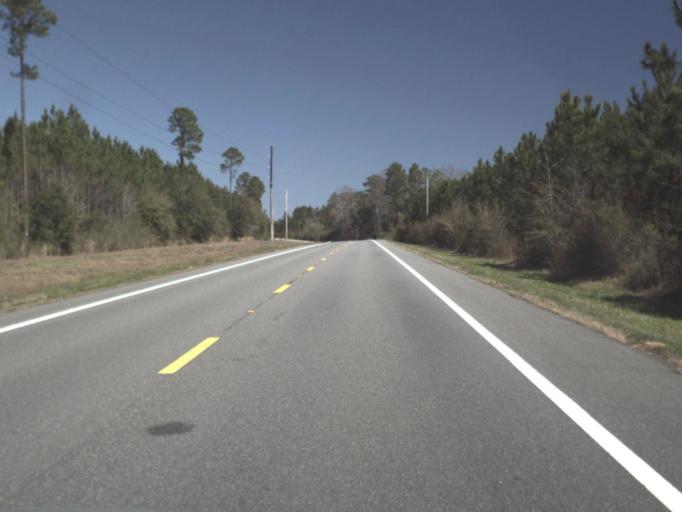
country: US
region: Florida
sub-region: Gadsden County
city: Quincy
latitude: 30.3999
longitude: -84.6748
